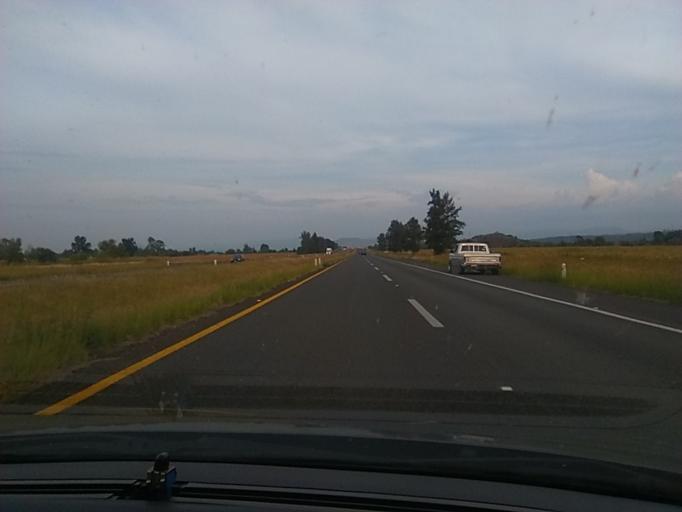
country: MX
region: Michoacan
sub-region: Alvaro Obregon
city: Tzintzimeo
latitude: 19.8912
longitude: -100.9947
